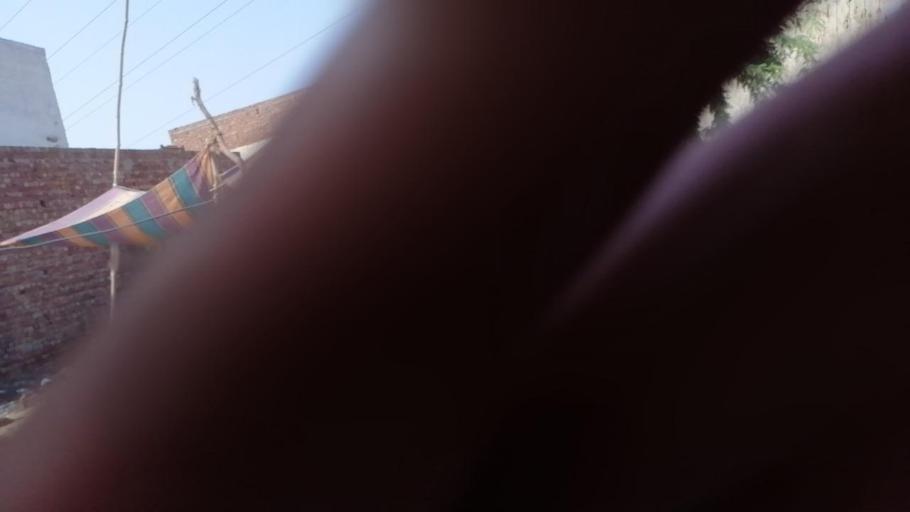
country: PK
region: Punjab
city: Kamalia
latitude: 30.7244
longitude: 72.6637
